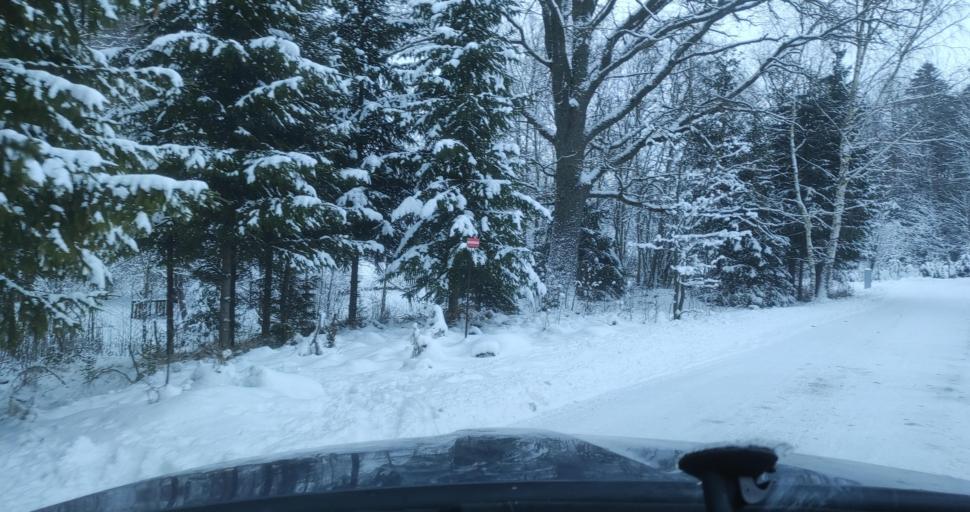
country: LV
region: Kuldigas Rajons
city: Kuldiga
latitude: 56.9914
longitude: 22.0468
